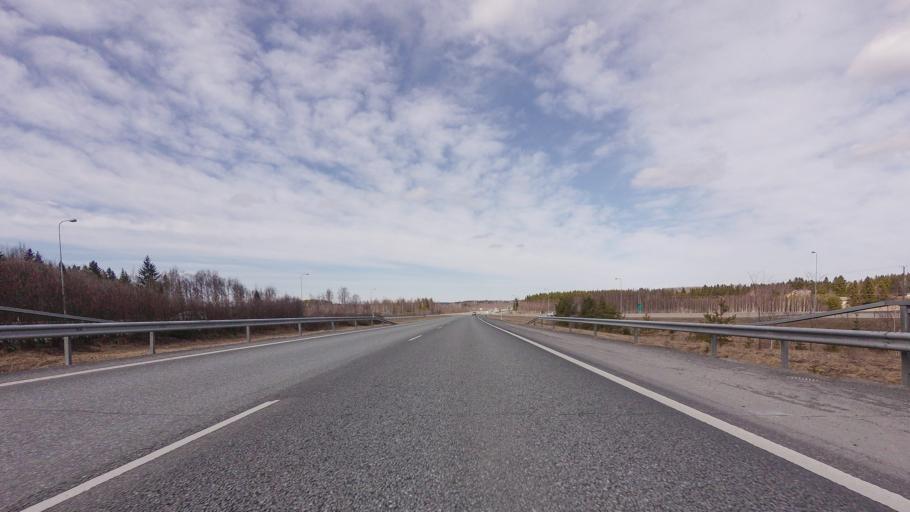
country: FI
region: Pirkanmaa
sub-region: Tampere
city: Lempaeaelae
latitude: 61.3359
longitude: 23.7943
